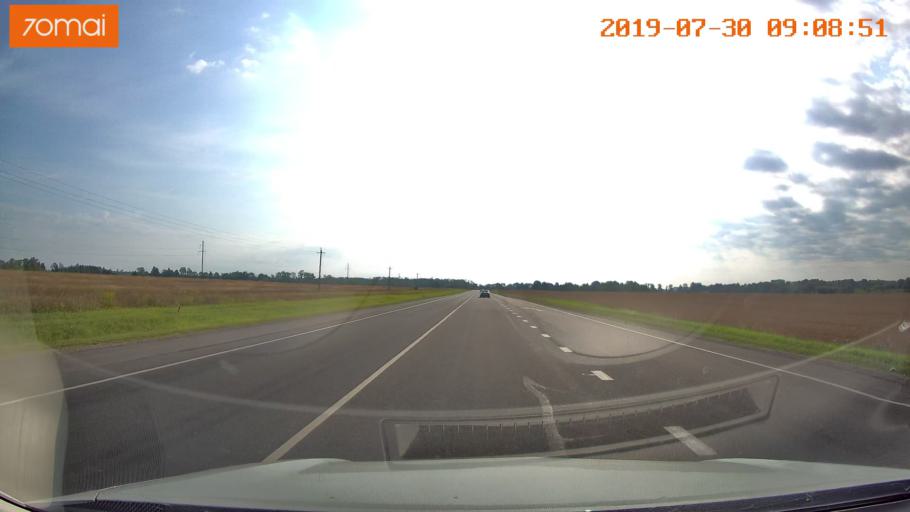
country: RU
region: Kaliningrad
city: Nesterov
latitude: 54.6135
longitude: 22.3949
